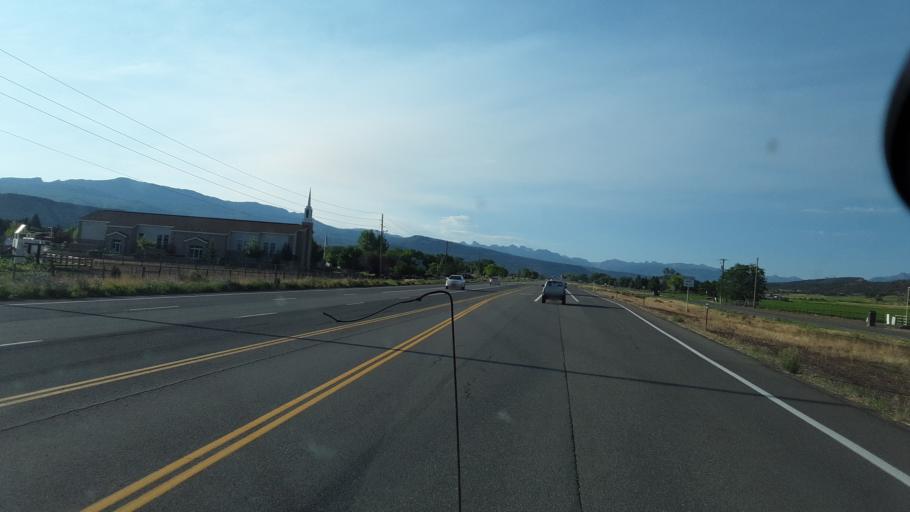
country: US
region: Colorado
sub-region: Montrose County
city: Montrose
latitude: 38.3795
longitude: -107.8202
